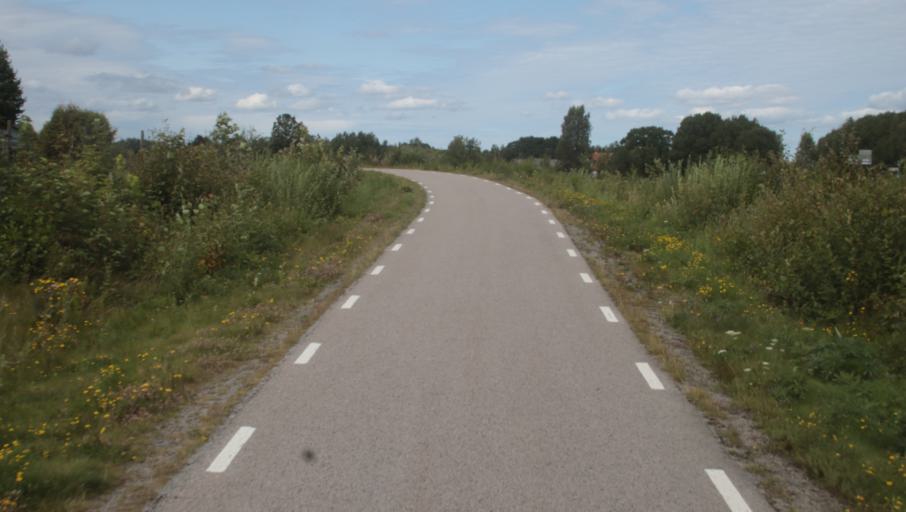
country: SE
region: Blekinge
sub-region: Karlshamns Kommun
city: Karlshamn
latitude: 56.2016
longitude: 14.8110
